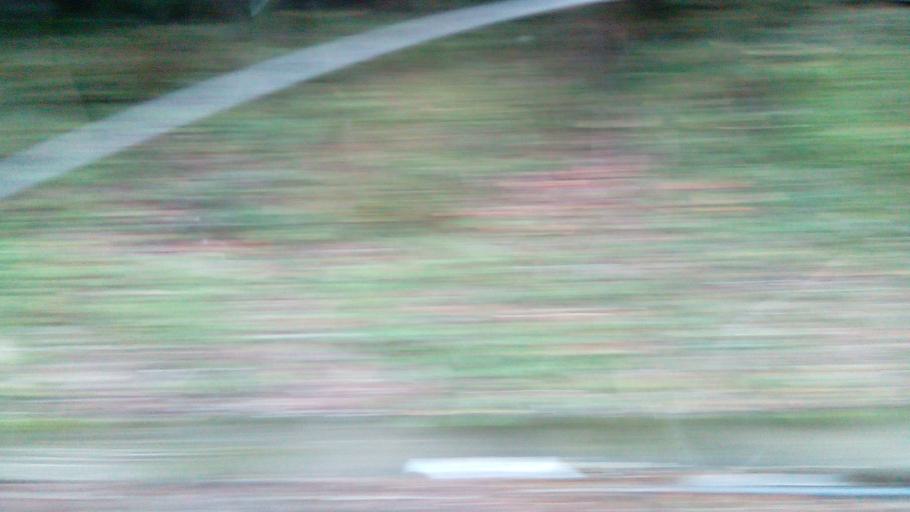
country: TW
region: Taiwan
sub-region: Hualien
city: Hualian
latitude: 24.3499
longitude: 121.3243
